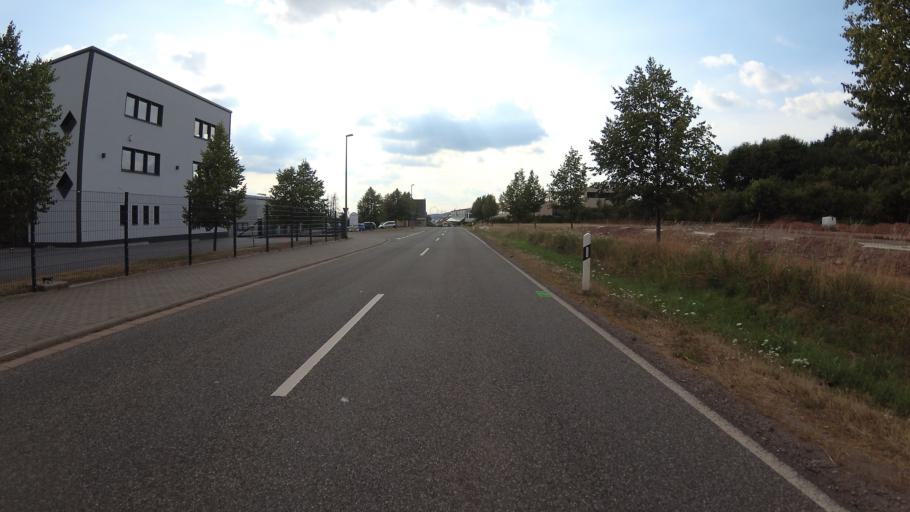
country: DE
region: Saarland
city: Eppelborn
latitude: 49.3723
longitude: 6.9946
